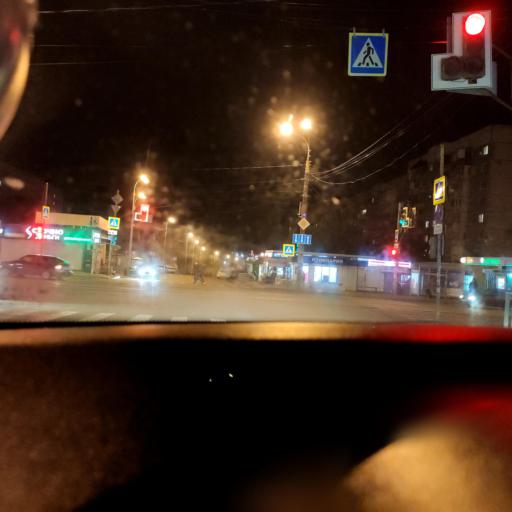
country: RU
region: Samara
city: Samara
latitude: 53.1917
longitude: 50.1415
